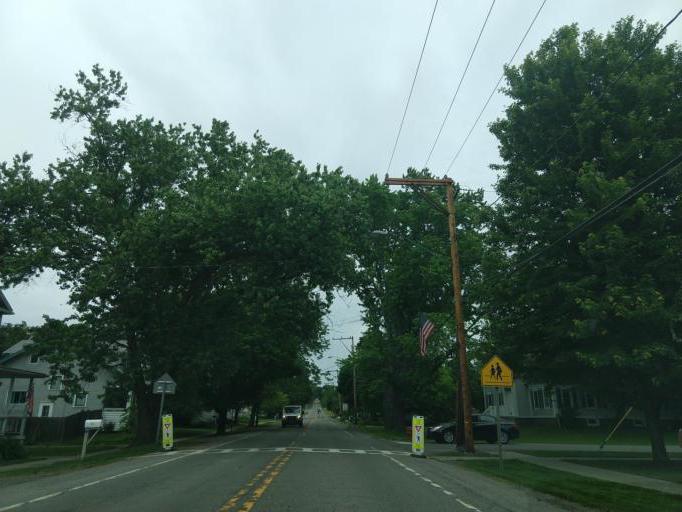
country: US
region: New York
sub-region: Tompkins County
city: Dryden
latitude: 42.4906
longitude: -76.2950
